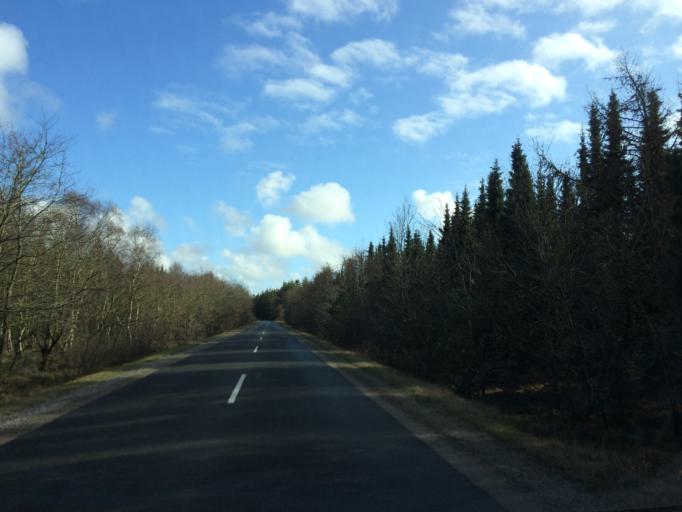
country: DK
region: Central Jutland
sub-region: Holstebro Kommune
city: Ulfborg
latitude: 56.2636
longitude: 8.3391
